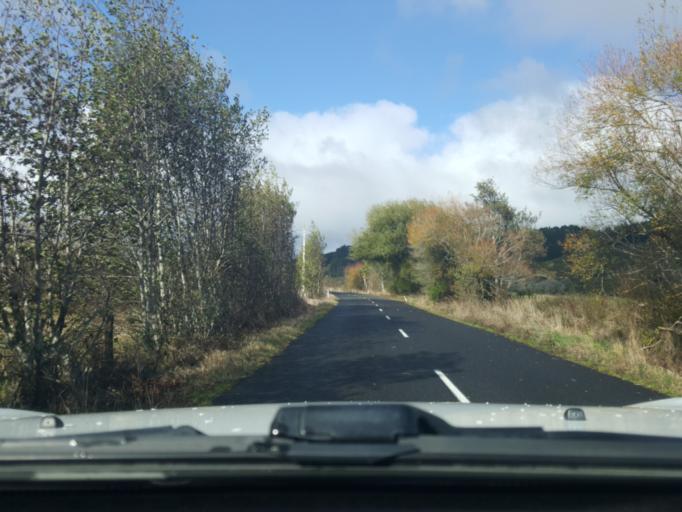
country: NZ
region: Waikato
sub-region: Waikato District
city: Te Kauwhata
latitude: -37.3883
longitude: 175.0559
